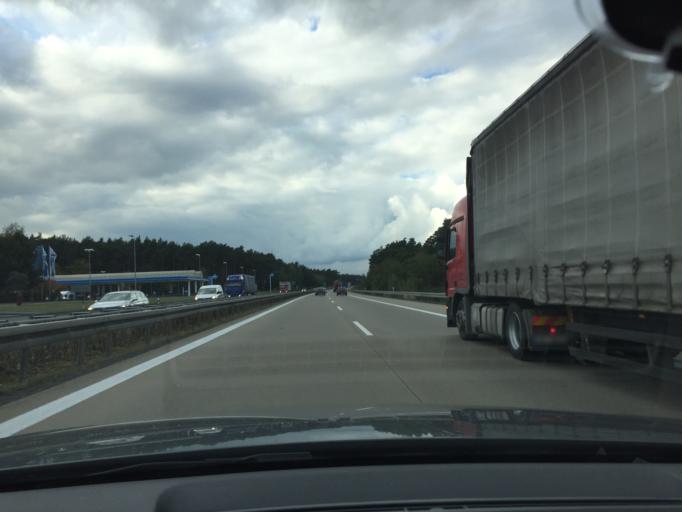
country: DE
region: Brandenburg
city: Luebben
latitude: 51.8887
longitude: 13.8404
